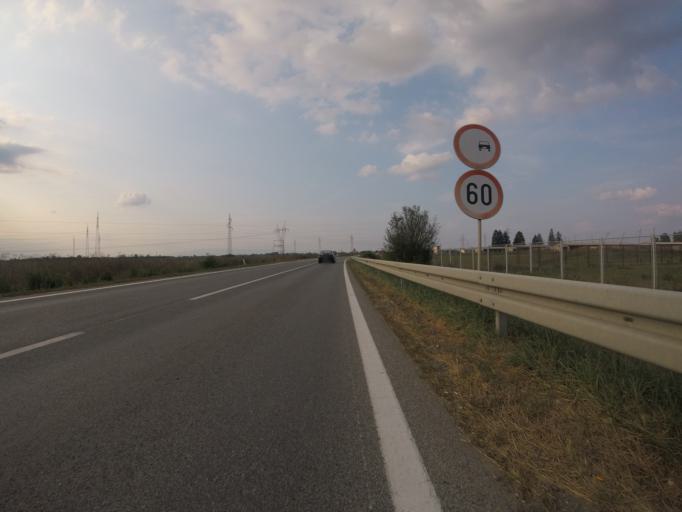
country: HR
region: Zagrebacka
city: Mraclin
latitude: 45.6697
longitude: 16.1176
